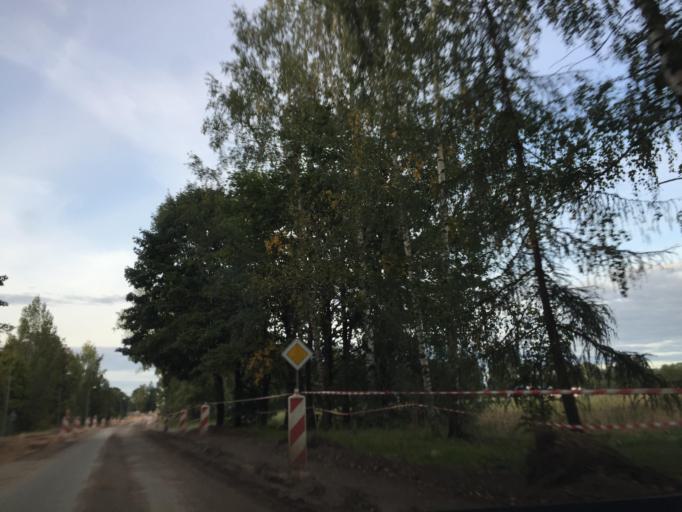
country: LV
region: Salas
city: Sala
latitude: 56.4056
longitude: 25.7709
